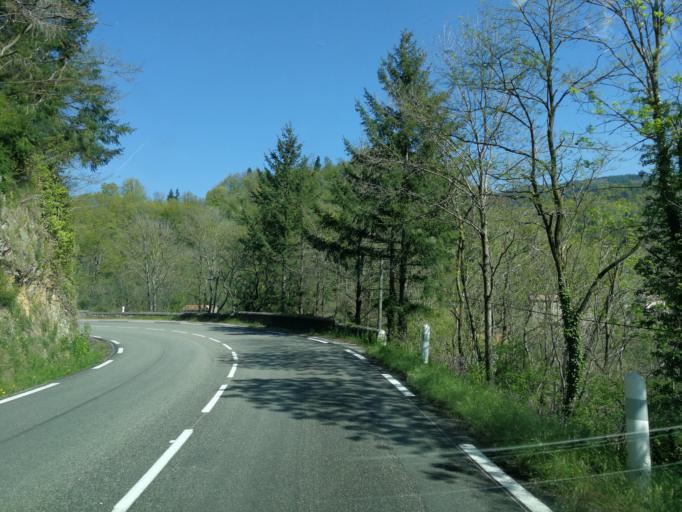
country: FR
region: Rhone-Alpes
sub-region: Departement de l'Ardeche
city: Le Cheylard
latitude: 44.9043
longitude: 4.4831
